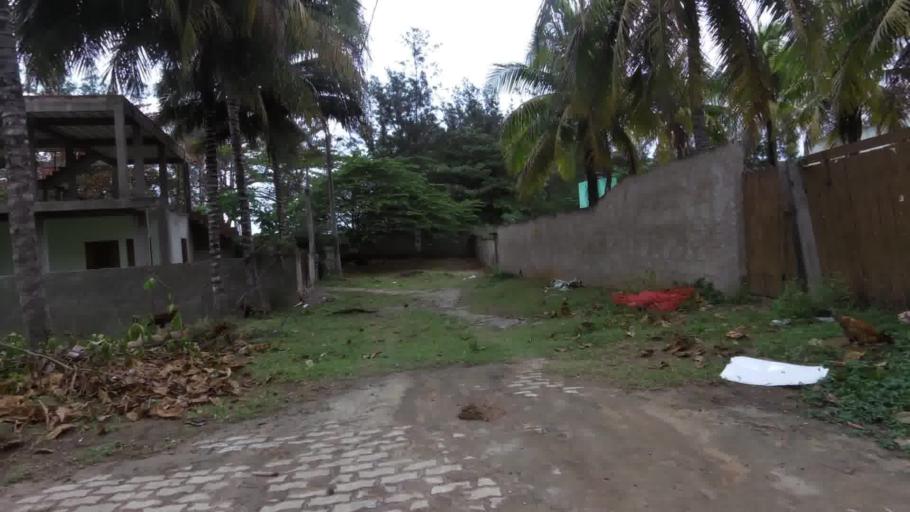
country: BR
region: Espirito Santo
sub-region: Marataizes
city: Marataizes
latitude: -21.0716
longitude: -40.8381
